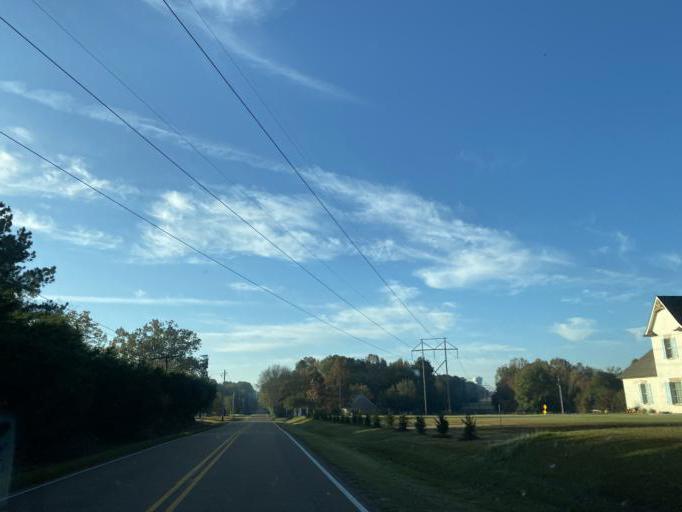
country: US
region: Mississippi
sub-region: Madison County
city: Madison
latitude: 32.4801
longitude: -90.0718
